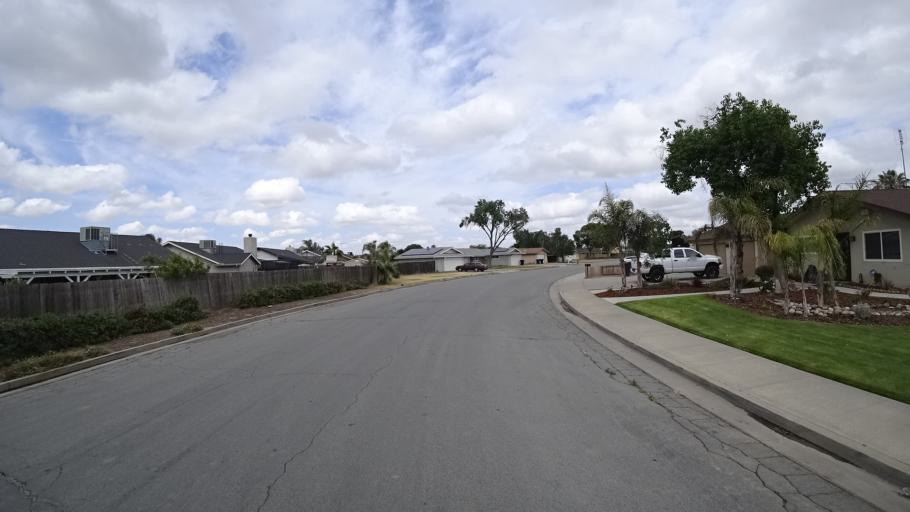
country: US
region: California
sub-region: Kings County
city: Home Garden
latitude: 36.3020
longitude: -119.6552
